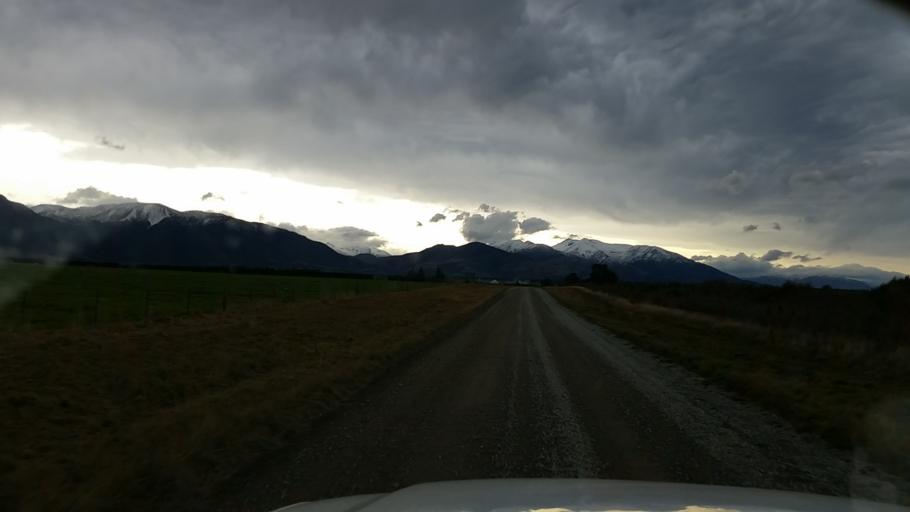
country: NZ
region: Canterbury
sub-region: Ashburton District
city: Methven
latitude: -43.7049
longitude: 171.4599
